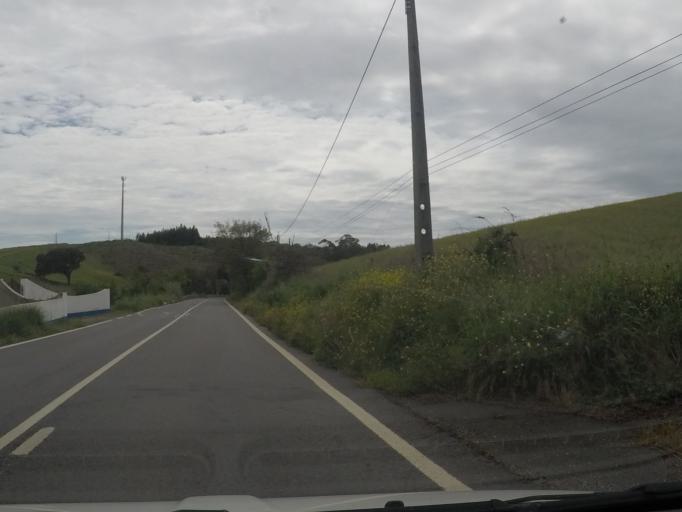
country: PT
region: Setubal
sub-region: Sines
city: Porto Covo
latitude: 37.8667
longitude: -8.7271
